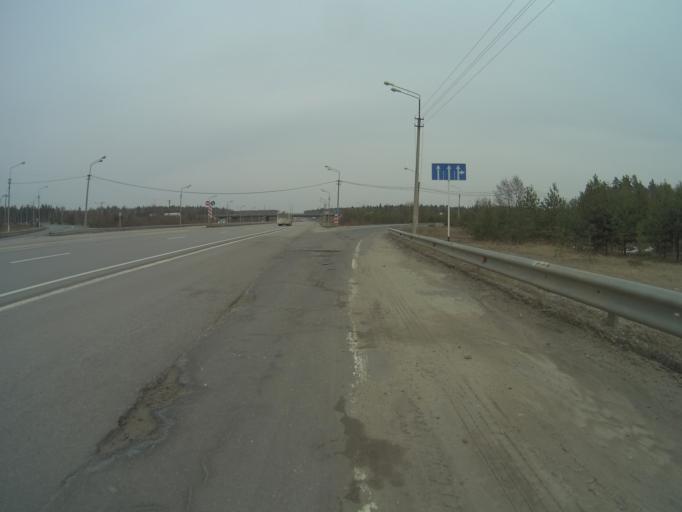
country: RU
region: Vladimir
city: Kommunar
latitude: 56.0815
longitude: 40.4692
